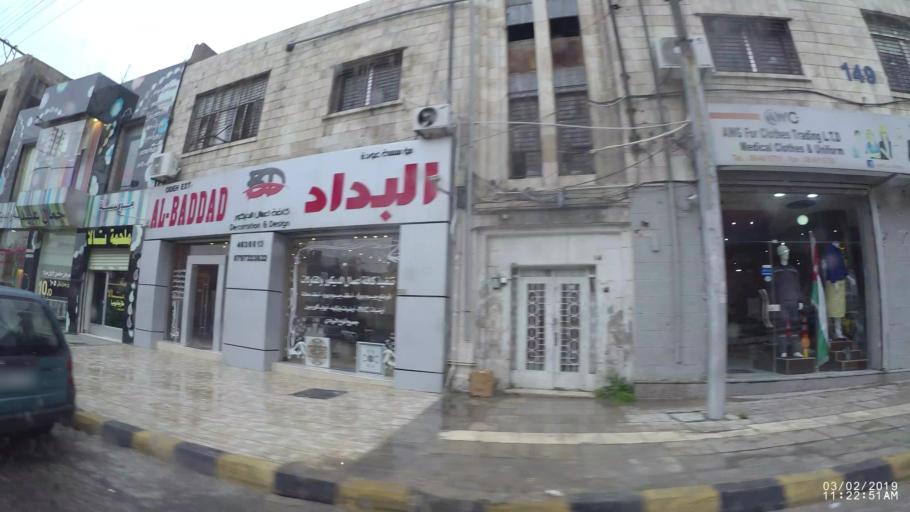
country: JO
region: Amman
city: Amman
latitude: 31.9534
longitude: 35.9236
